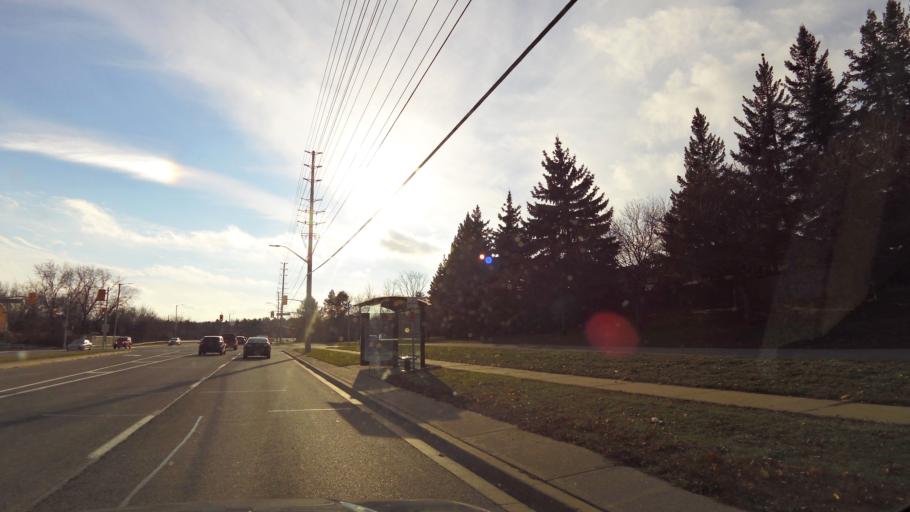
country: CA
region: Ontario
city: Mississauga
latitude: 43.5512
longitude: -79.6766
